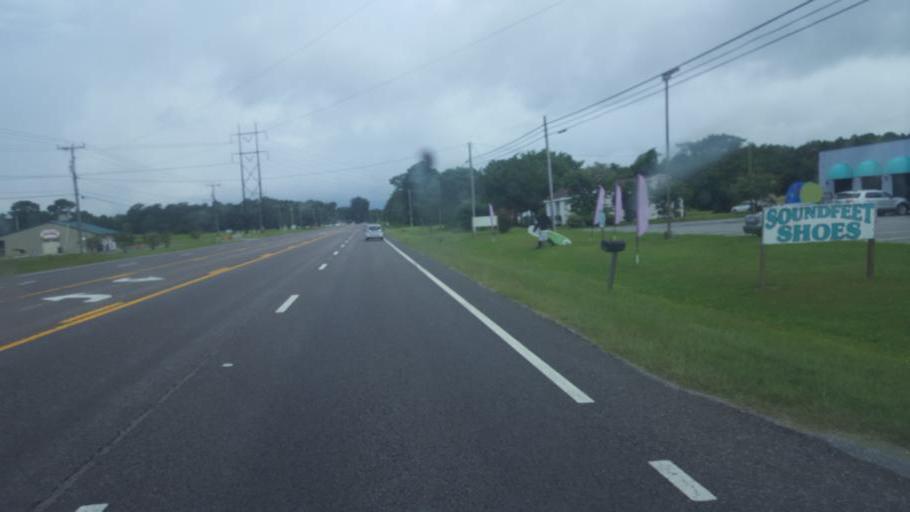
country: US
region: North Carolina
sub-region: Dare County
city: Southern Shores
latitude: 36.1459
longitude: -75.8473
